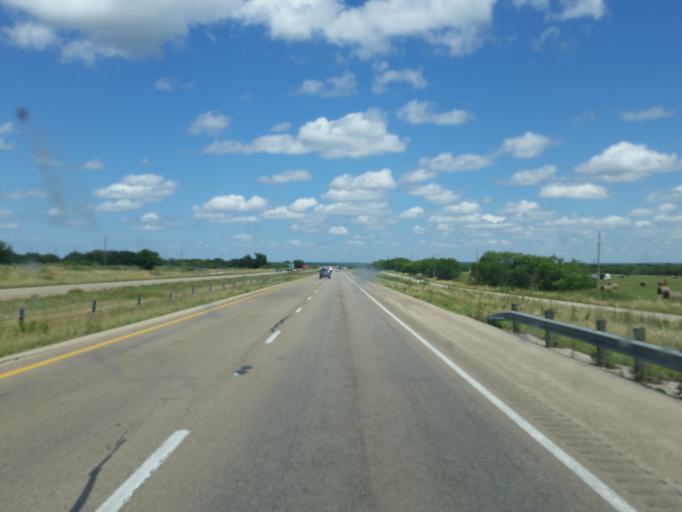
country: US
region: Texas
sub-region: Callahan County
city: Baird
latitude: 32.3896
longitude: -99.3303
